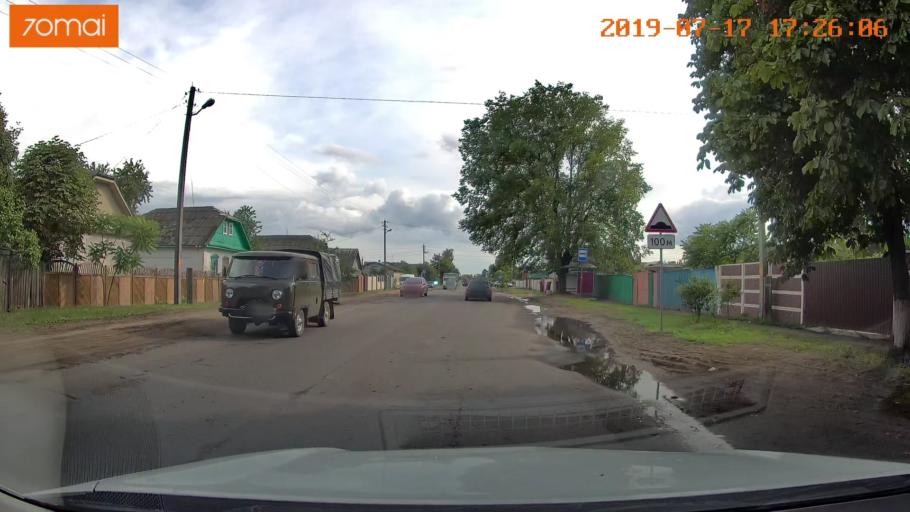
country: BY
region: Mogilev
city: Babruysk
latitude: 53.1431
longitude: 29.1734
